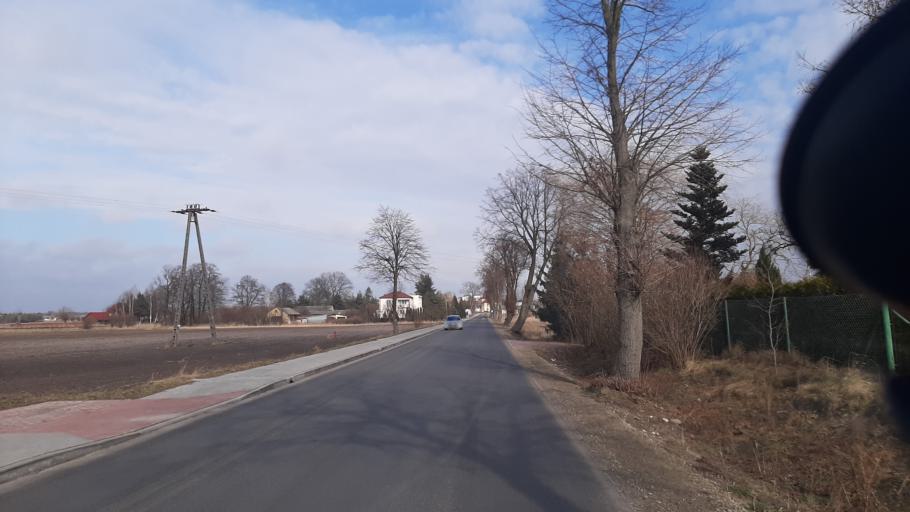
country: PL
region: Lublin Voivodeship
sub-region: Powiat lubartowski
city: Serniki
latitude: 51.4482
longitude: 22.6685
